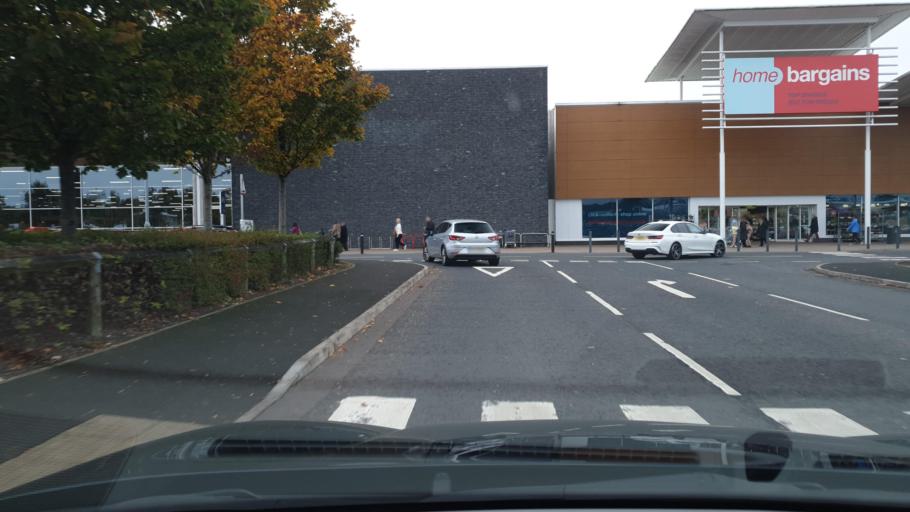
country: GB
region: Northern Ireland
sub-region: Banbridge District
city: Banbridge
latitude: 54.3334
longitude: -6.2738
